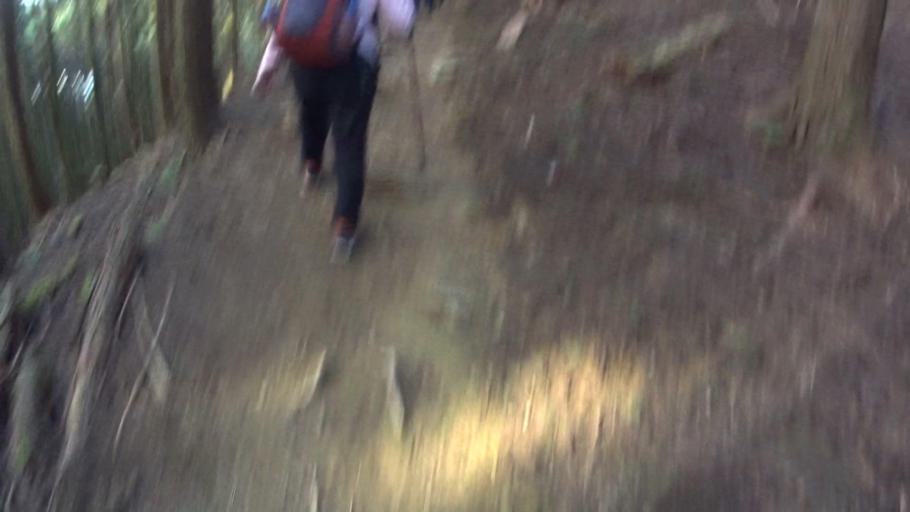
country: JP
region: Shiga Prefecture
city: Kitahama
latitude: 35.1028
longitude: 135.8434
